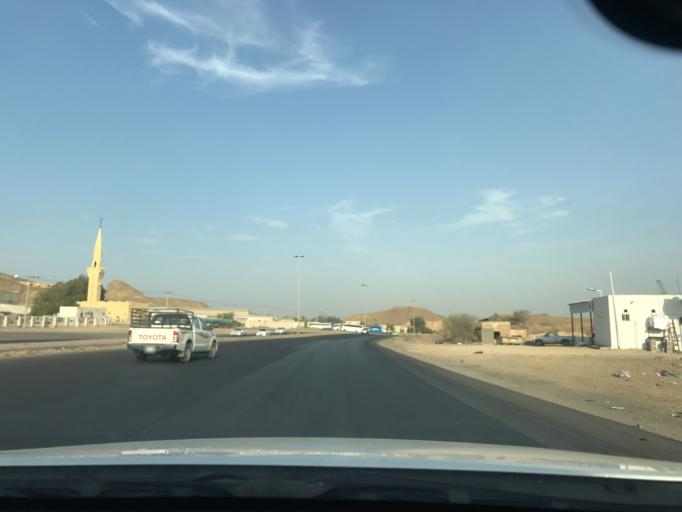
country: SA
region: Makkah
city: Jeddah
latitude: 21.4121
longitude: 39.4205
